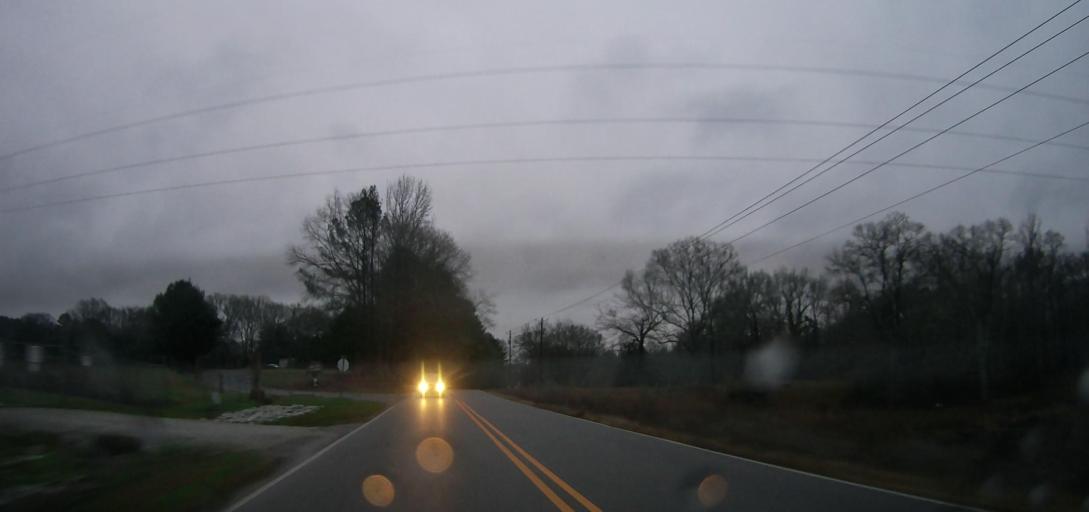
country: US
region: Alabama
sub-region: Tuscaloosa County
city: Vance
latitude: 33.1199
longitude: -87.2238
